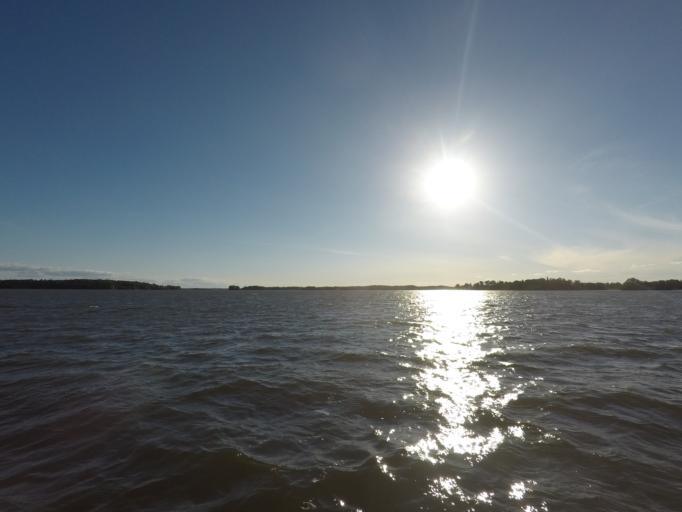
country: SE
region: Vaestmanland
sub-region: Vasteras
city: Vasteras
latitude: 59.5057
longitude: 16.5444
